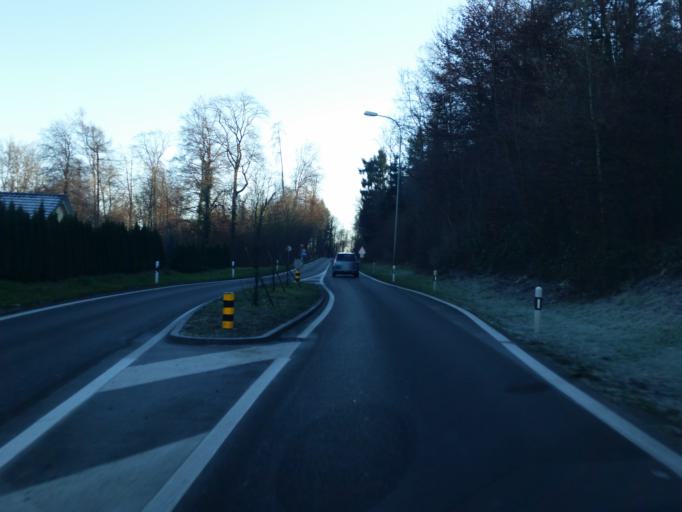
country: CH
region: Aargau
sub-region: Bezirk Baden
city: Kunten
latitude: 47.3651
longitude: 8.3153
